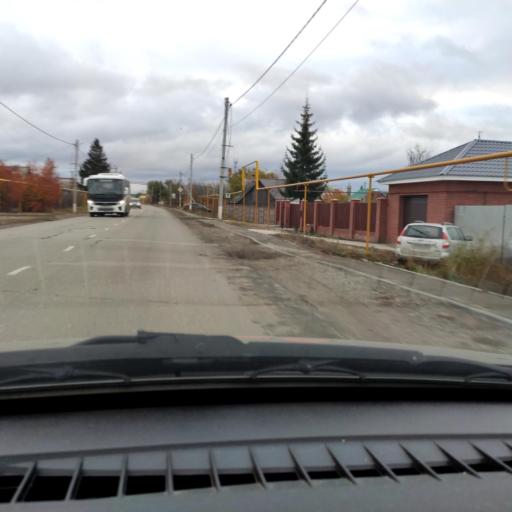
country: RU
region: Samara
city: Podstepki
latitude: 53.5160
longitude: 49.1262
